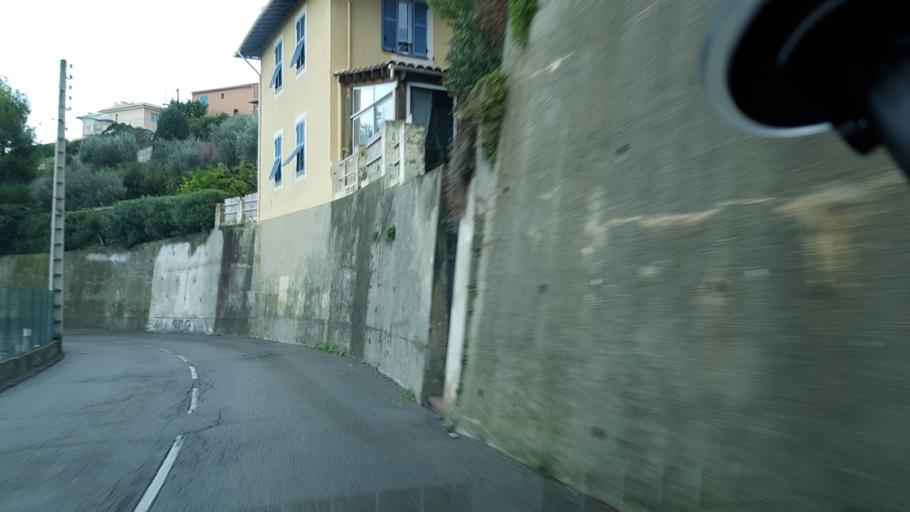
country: FR
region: Provence-Alpes-Cote d'Azur
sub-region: Departement des Alpes-Maritimes
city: Nice
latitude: 43.7025
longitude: 7.2310
